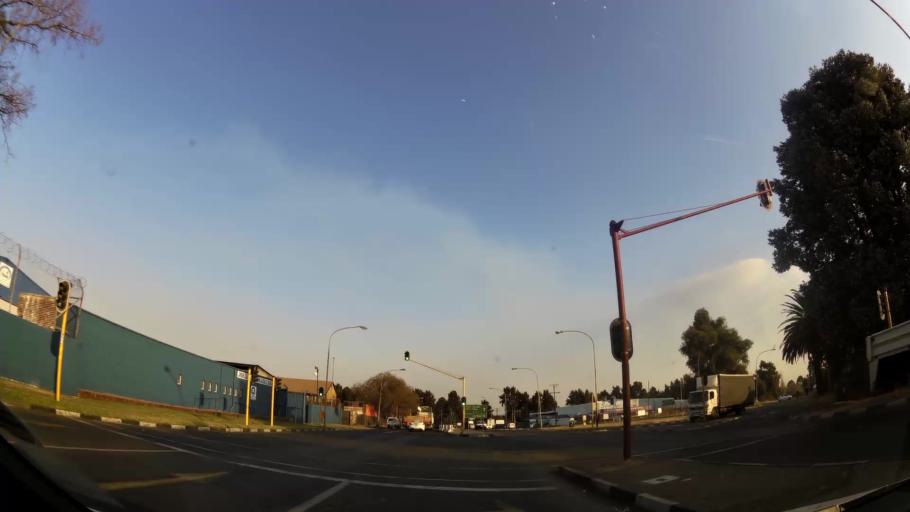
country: ZA
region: Gauteng
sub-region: Ekurhuleni Metropolitan Municipality
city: Springs
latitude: -26.2630
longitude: 28.4189
